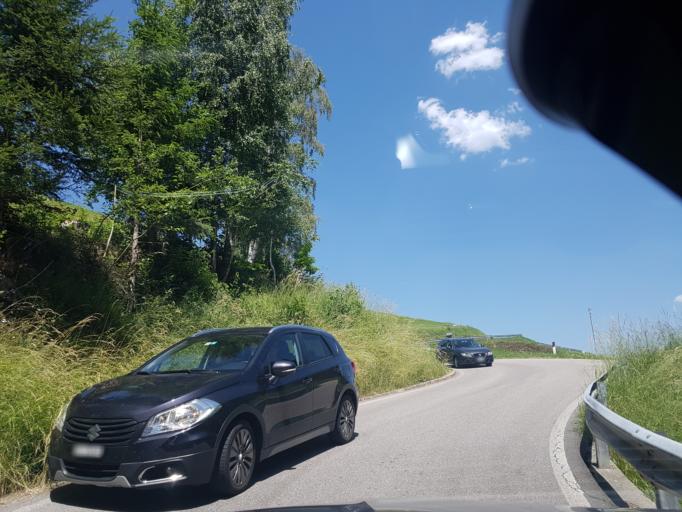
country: IT
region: Trentino-Alto Adige
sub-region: Bolzano
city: Villandro - Villanders
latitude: 46.6347
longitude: 11.5270
